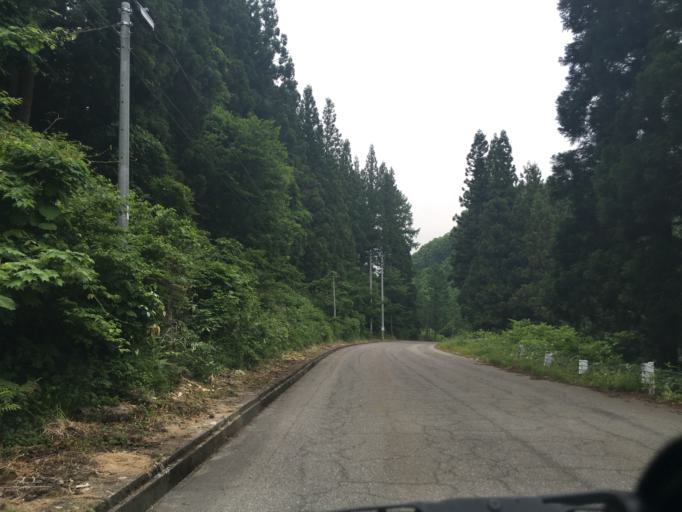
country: JP
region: Fukushima
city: Kitakata
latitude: 37.4881
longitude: 139.7374
